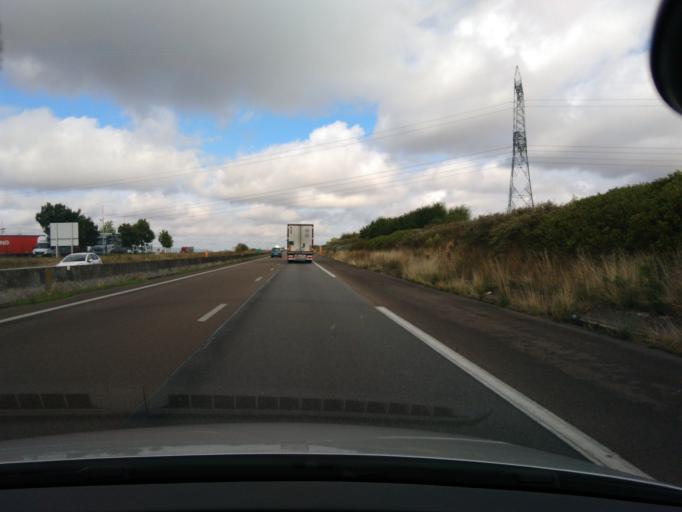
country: FR
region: Haute-Normandie
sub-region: Departement de l'Eure
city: La Madeleine-de-Nonancourt
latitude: 48.8535
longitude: 1.1796
